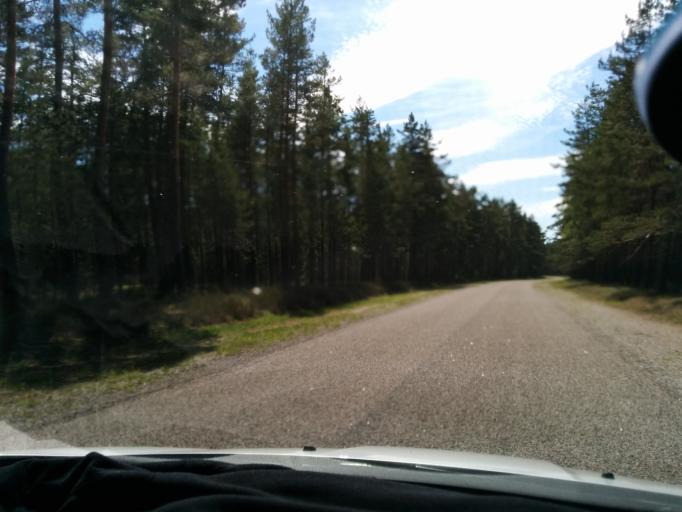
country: EE
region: Harju
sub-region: Loksa linn
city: Loksa
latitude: 59.5471
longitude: 25.9843
